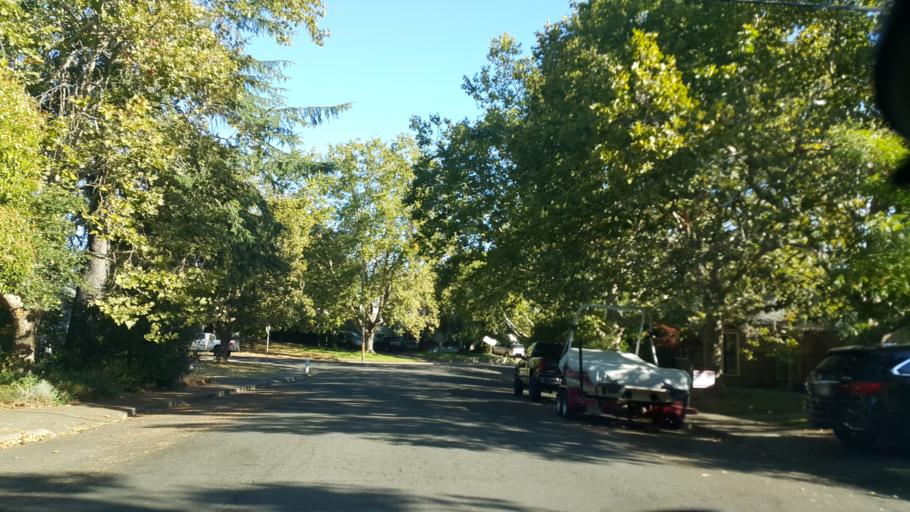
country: US
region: California
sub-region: Mendocino County
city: Ukiah
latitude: 39.1425
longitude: -123.2138
